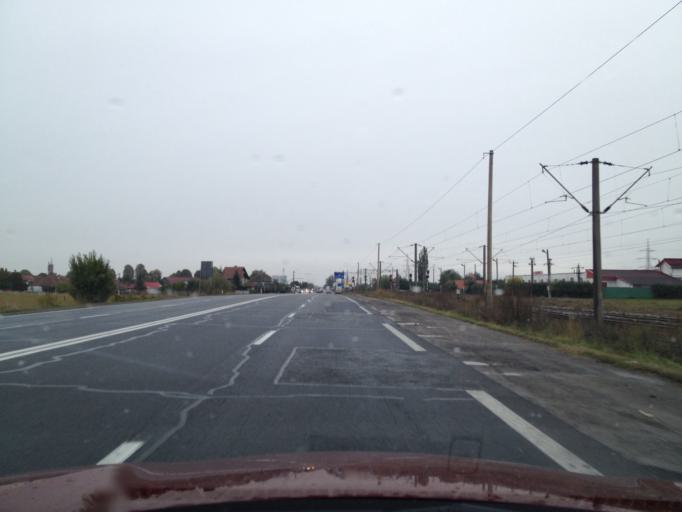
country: RO
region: Brasov
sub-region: Comuna Harman
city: Harman
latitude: 45.6984
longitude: 25.6865
